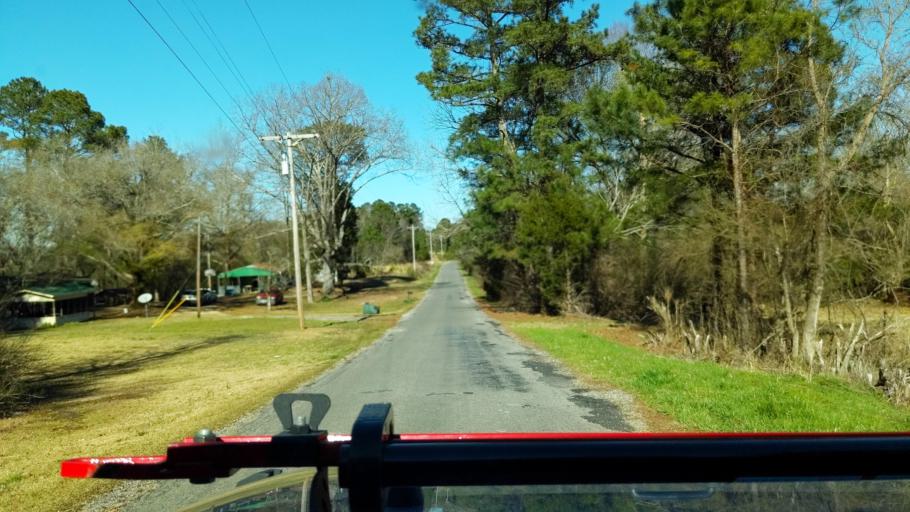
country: US
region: Alabama
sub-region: Walker County
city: Jasper
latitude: 34.0516
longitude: -87.1551
